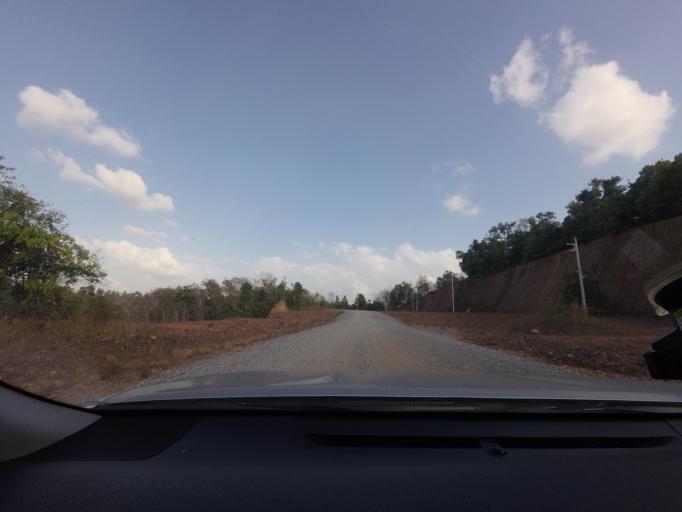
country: TH
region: Pattani
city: Mae Lan
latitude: 6.6061
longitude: 101.2432
